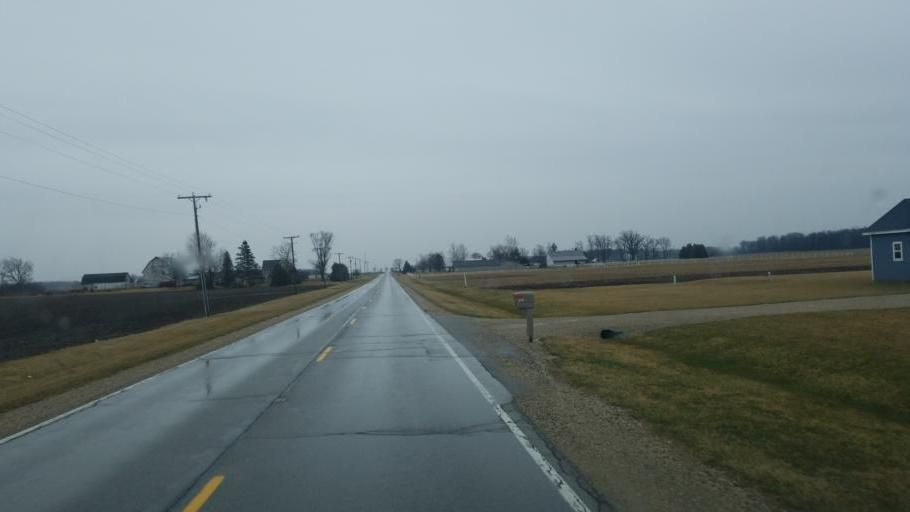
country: US
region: Indiana
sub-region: Adams County
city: Geneva
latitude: 40.6169
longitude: -85.0411
